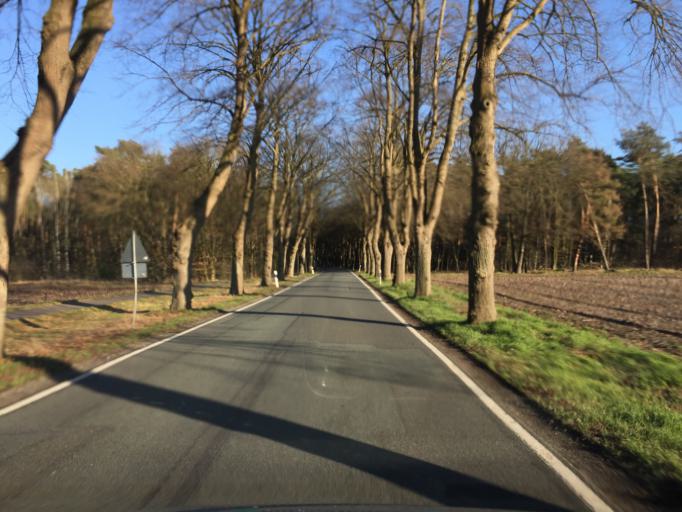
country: DE
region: Lower Saxony
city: Husum
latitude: 52.5545
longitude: 9.2354
